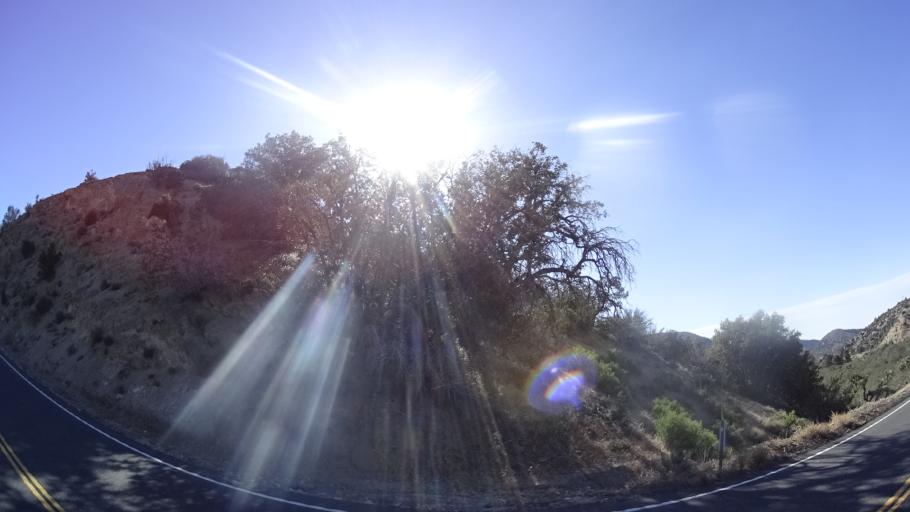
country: US
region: California
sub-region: San Bernardino County
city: Wrightwood
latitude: 34.3651
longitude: -117.6033
